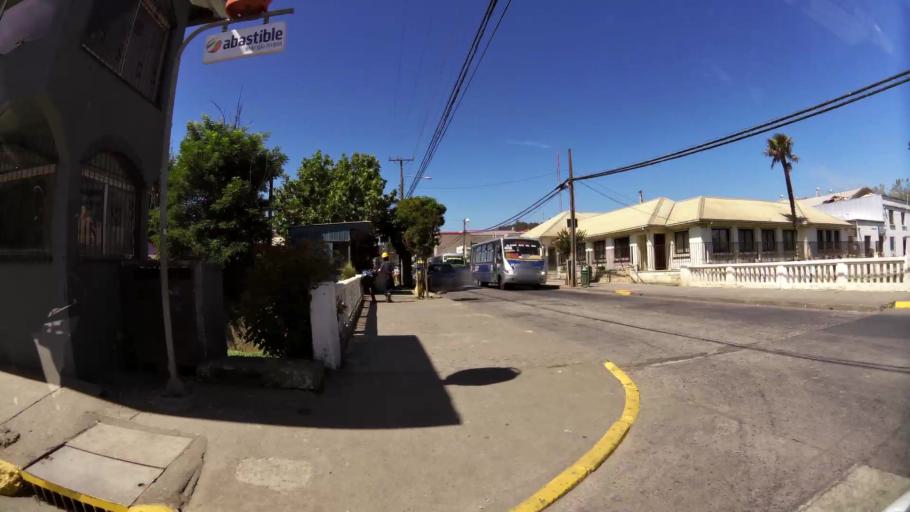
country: CL
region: Biobio
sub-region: Provincia de Concepcion
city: Penco
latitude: -36.7374
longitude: -72.9953
